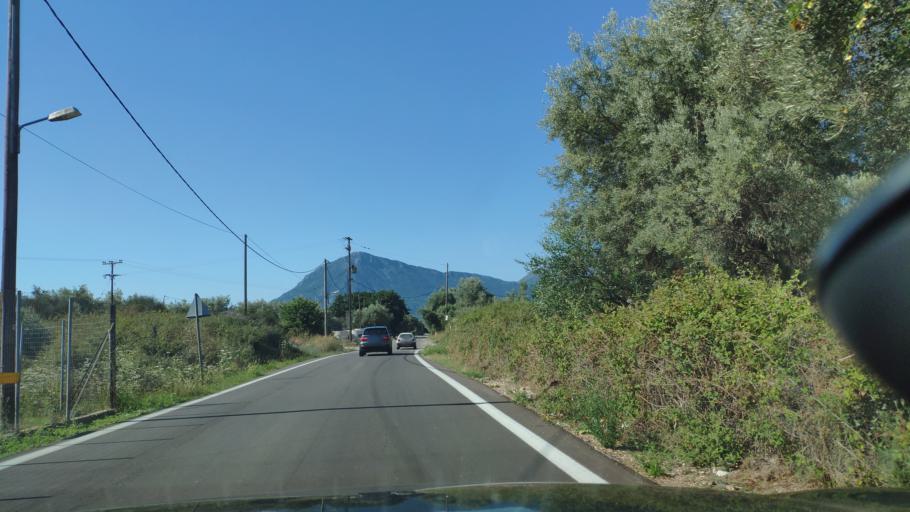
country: GR
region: West Greece
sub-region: Nomos Aitolias kai Akarnanias
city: Kandila
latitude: 38.6998
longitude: 20.9482
